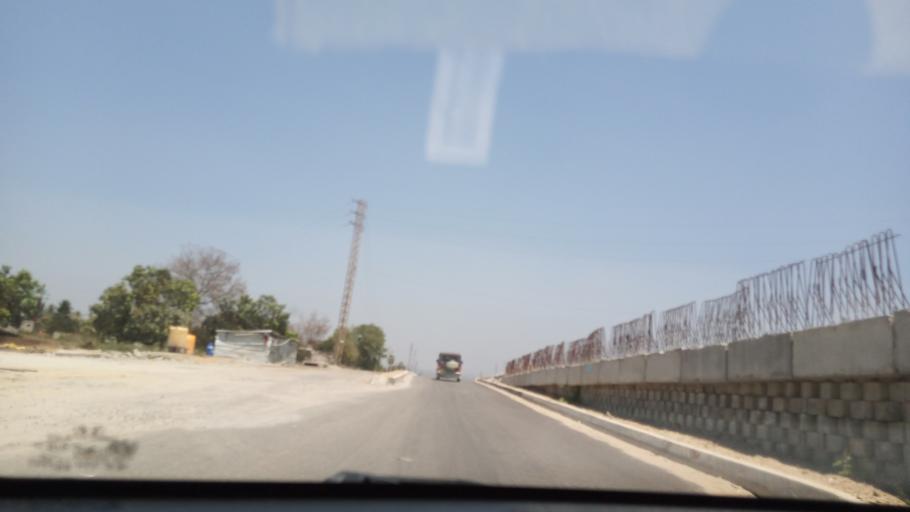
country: IN
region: Andhra Pradesh
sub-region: Chittoor
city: Pakala
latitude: 13.3570
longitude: 79.0860
